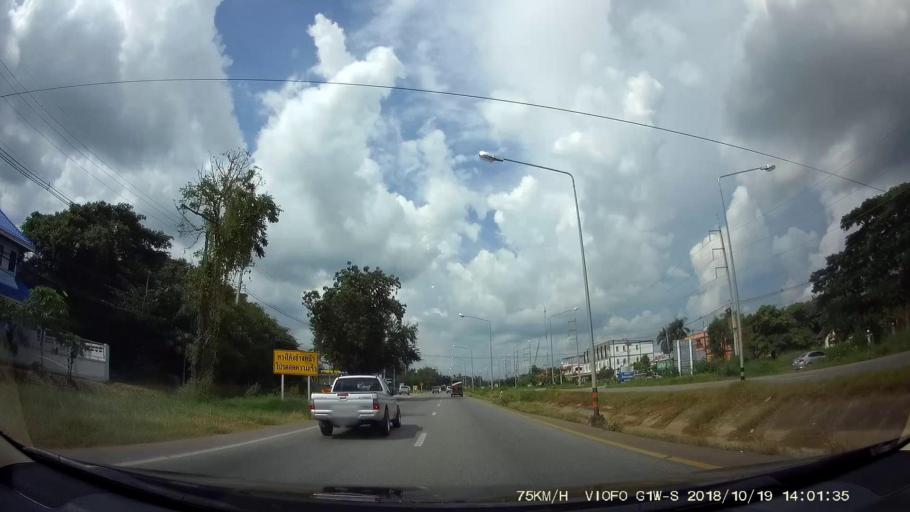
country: TH
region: Chaiyaphum
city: Chaiyaphum
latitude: 15.8310
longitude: 102.0586
